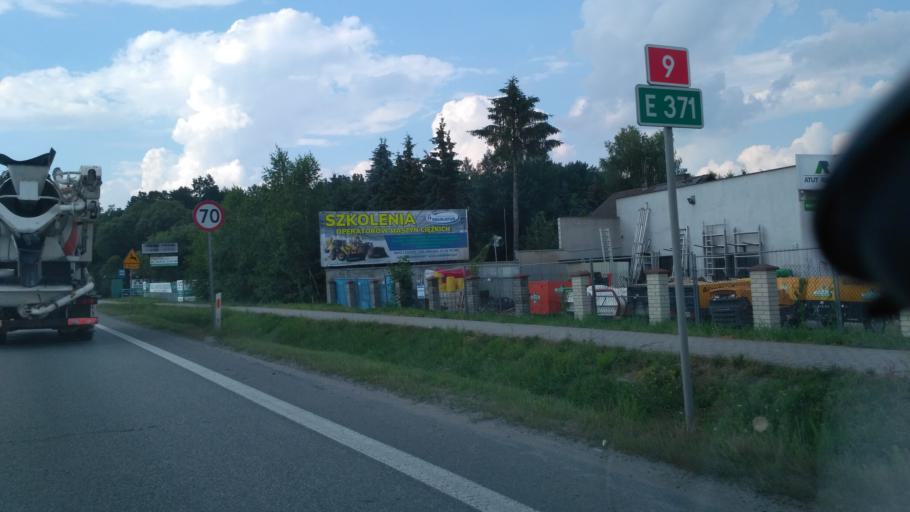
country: PL
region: Subcarpathian Voivodeship
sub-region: Powiat rzeszowski
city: Rudna Mala
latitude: 50.1175
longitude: 21.9720
